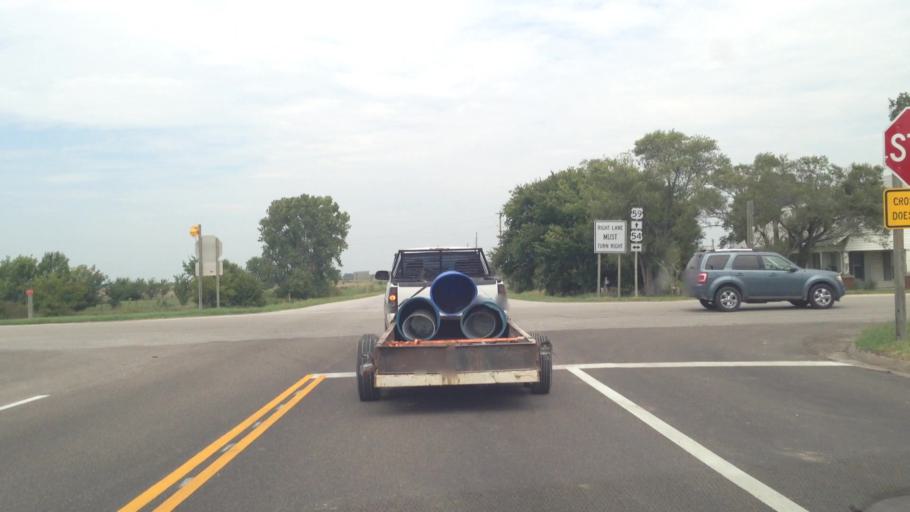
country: US
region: Kansas
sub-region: Allen County
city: Iola
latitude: 37.9214
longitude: -95.1700
